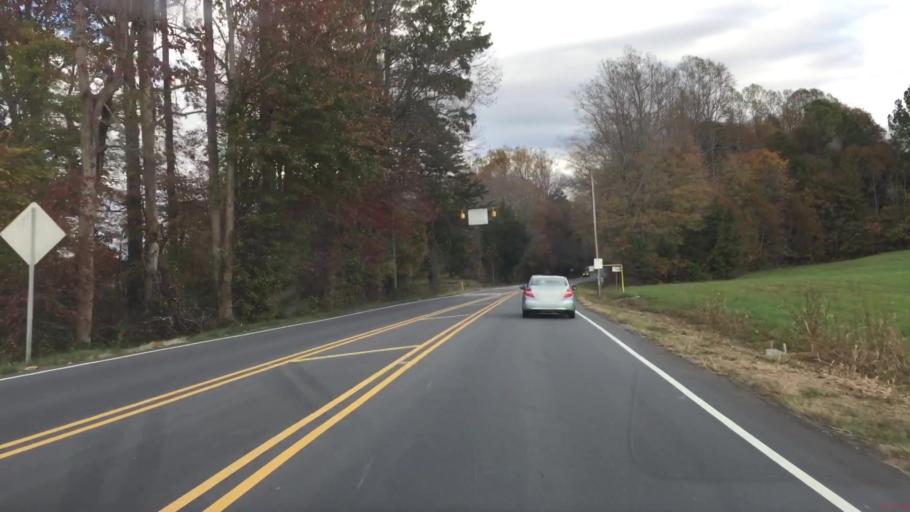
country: US
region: North Carolina
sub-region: Guilford County
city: Summerfield
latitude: 36.2623
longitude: -79.8659
